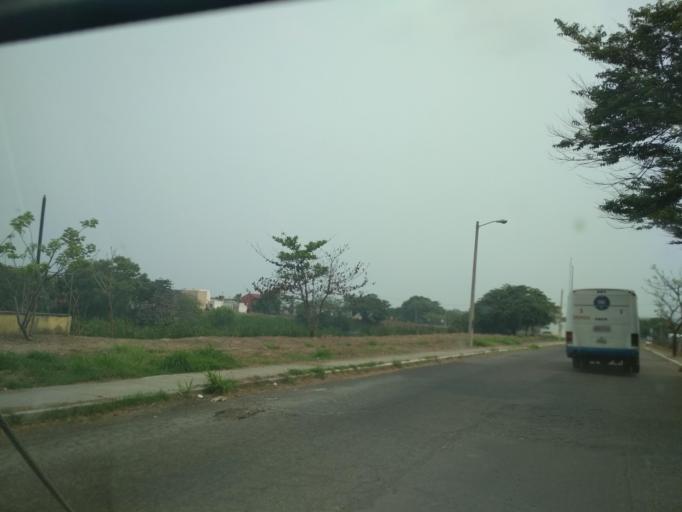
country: MX
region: Veracruz
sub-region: Veracruz
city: Fraccionamiento Geovillas los Pinos
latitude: 19.2180
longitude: -96.2240
